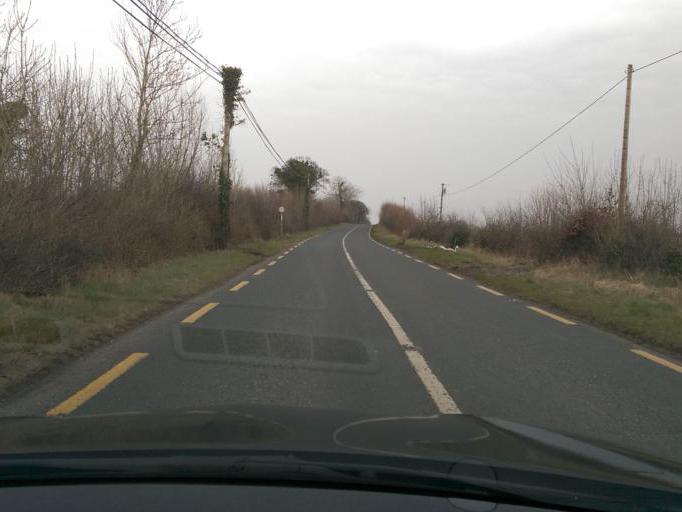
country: IE
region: Connaught
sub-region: Roscommon
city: Roscommon
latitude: 53.5121
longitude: -8.3591
